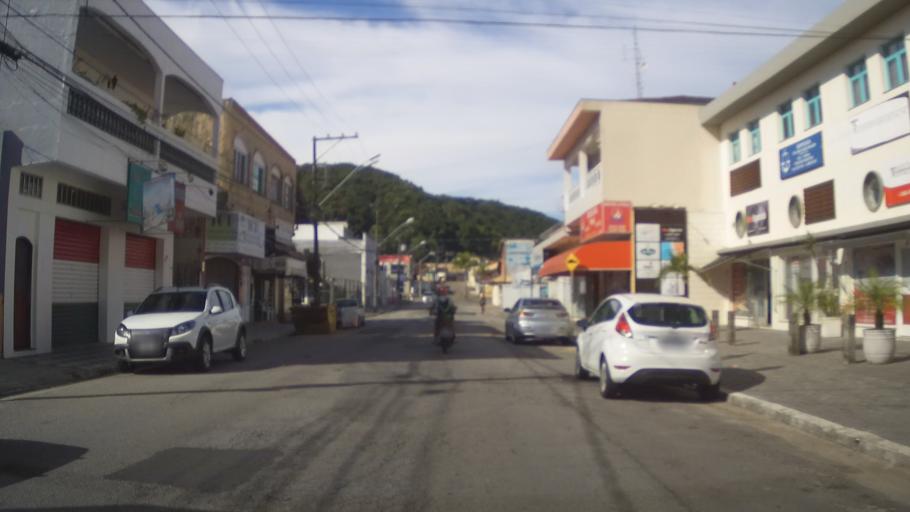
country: BR
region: Sao Paulo
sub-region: Itanhaem
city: Itanhaem
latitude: -24.1940
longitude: -46.8069
